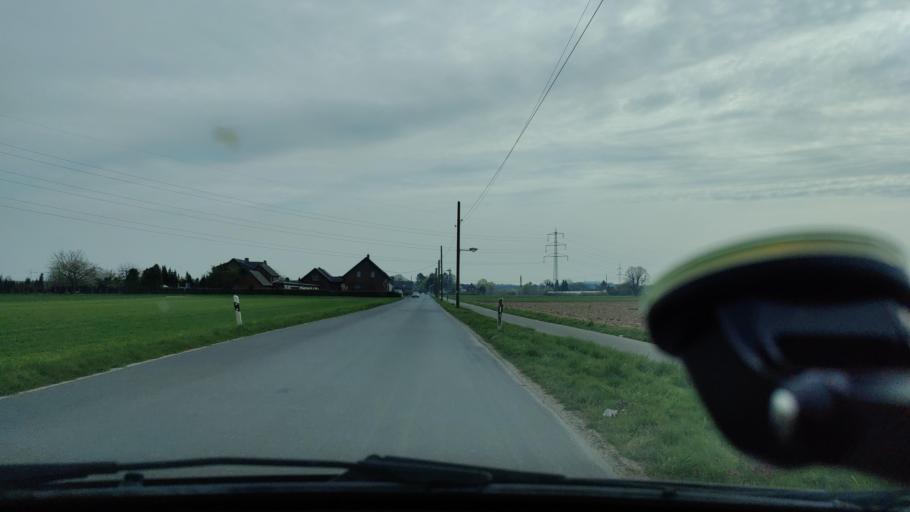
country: DE
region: North Rhine-Westphalia
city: Rheinberg
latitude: 51.5135
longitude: 6.6421
